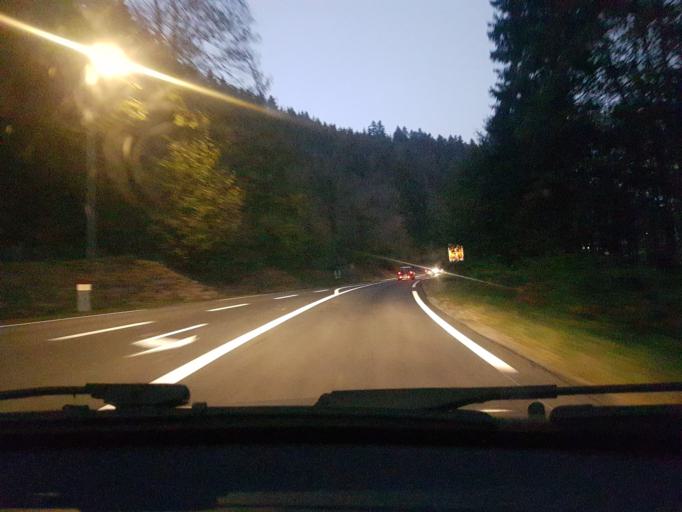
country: FR
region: Franche-Comte
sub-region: Departement du Doubs
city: Les Fins
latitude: 47.0759
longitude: 6.6179
